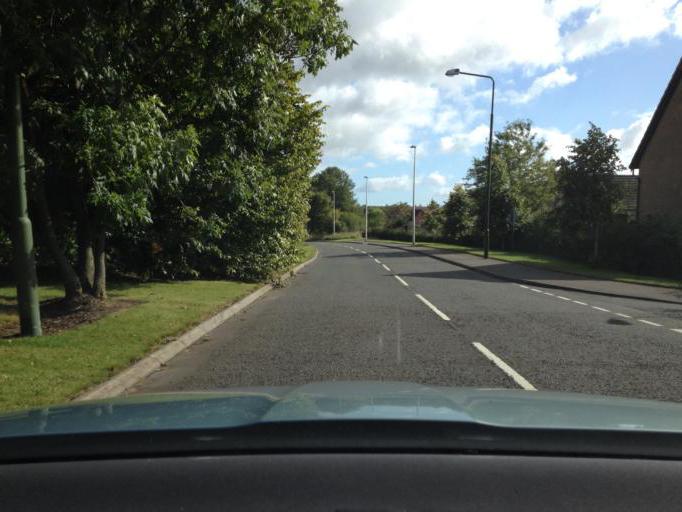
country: GB
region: Scotland
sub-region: West Lothian
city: Livingston
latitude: 55.8876
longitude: -3.5545
